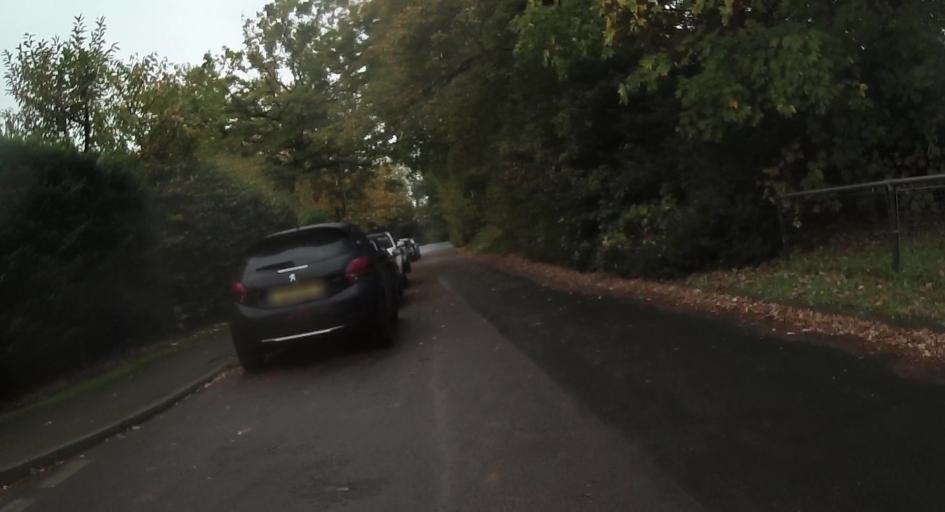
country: GB
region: England
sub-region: Surrey
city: Weybridge
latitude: 51.3586
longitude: -0.4624
